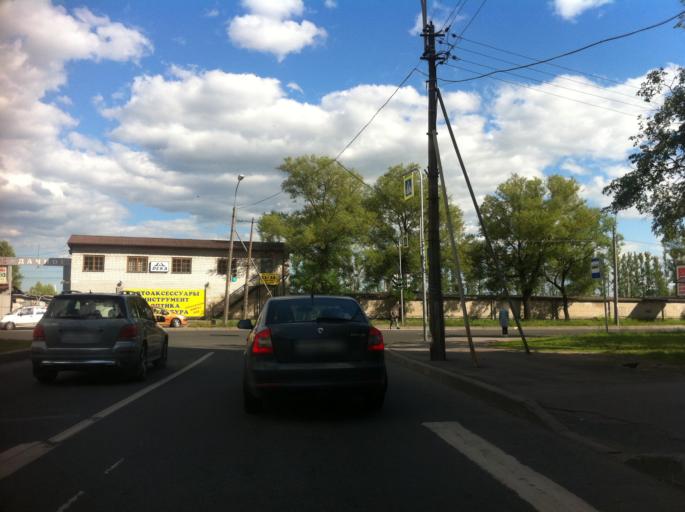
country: RU
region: St.-Petersburg
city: Dachnoye
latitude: 59.8401
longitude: 30.2724
